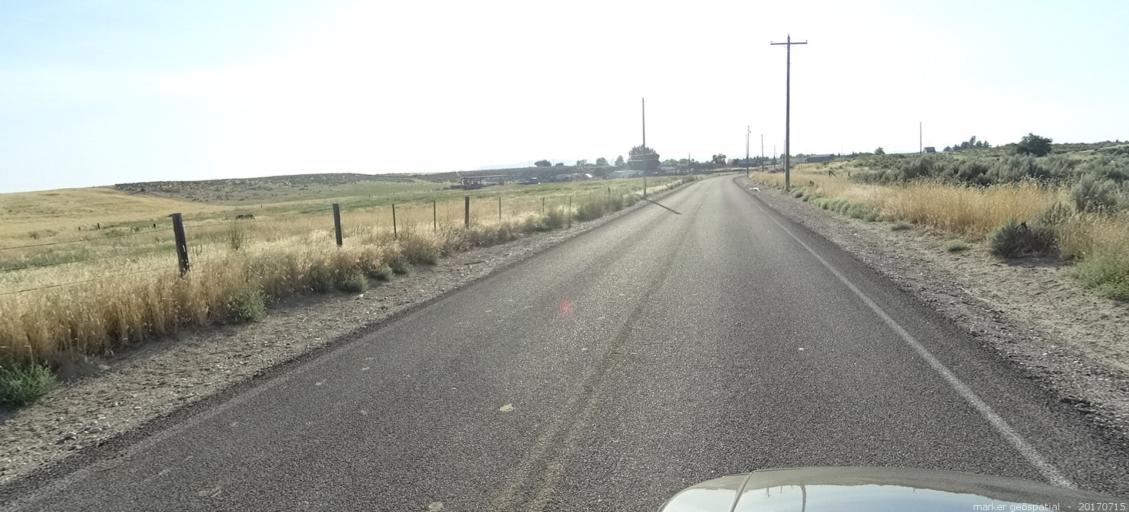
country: US
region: Idaho
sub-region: Ada County
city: Boise
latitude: 43.3894
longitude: -115.9779
